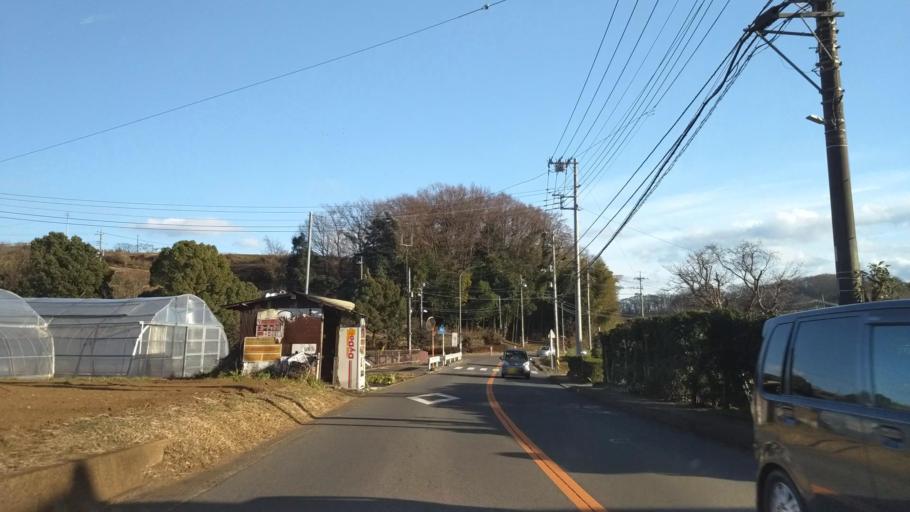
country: JP
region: Kanagawa
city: Oiso
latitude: 35.3469
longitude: 139.2796
